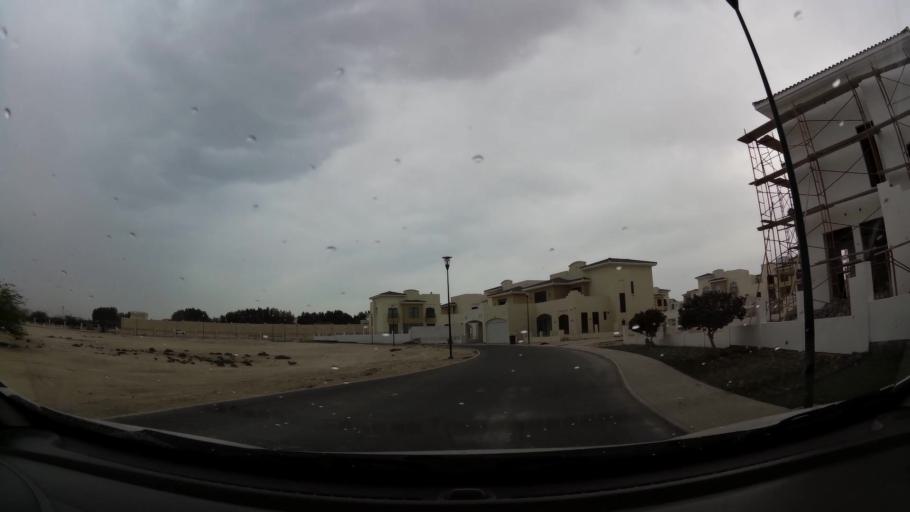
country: BH
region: Northern
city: Ar Rifa'
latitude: 26.0917
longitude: 50.5592
